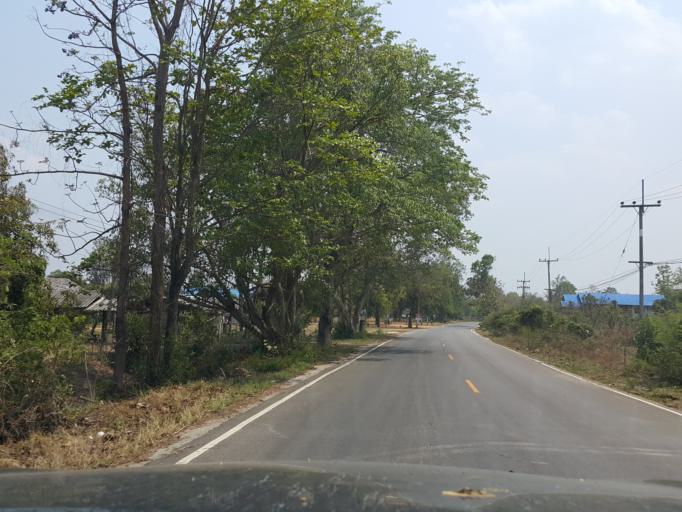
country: TH
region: Lampang
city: Mae Phrik
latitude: 17.4925
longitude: 99.1250
